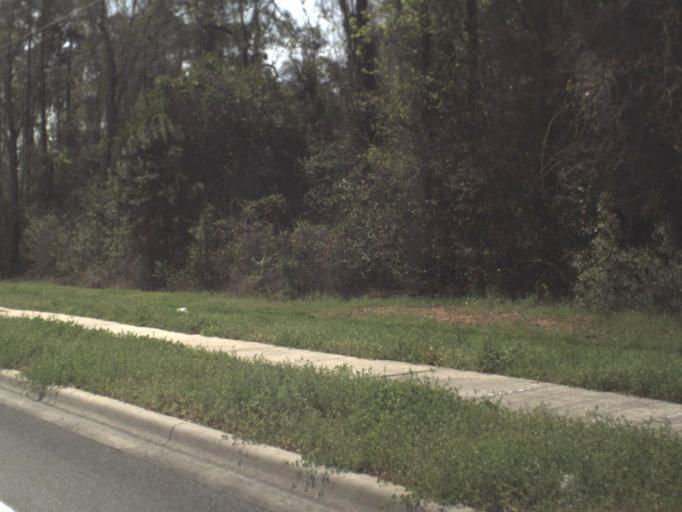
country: US
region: Florida
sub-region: Leon County
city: Tallahassee
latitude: 30.3949
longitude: -84.2352
